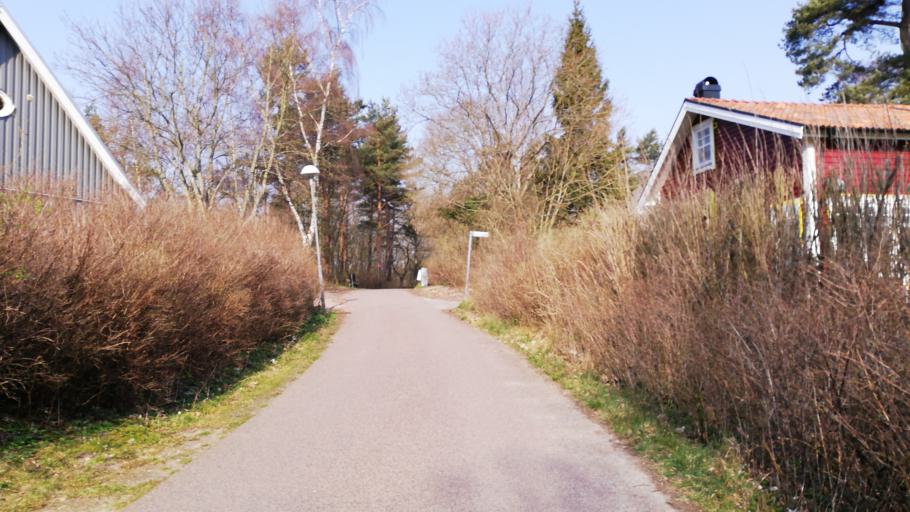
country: SE
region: Skane
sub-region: Ystads Kommun
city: Ystad
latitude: 55.4263
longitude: 13.8454
